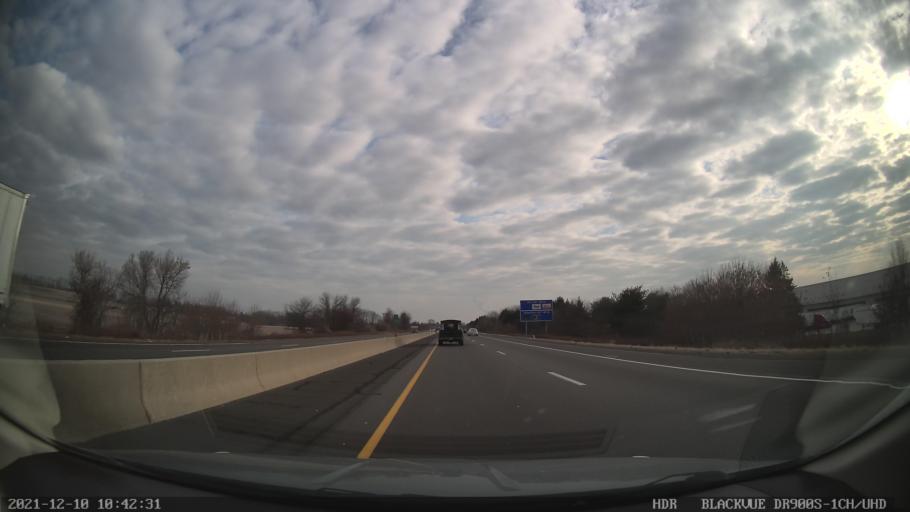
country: US
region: Pennsylvania
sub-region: Lehigh County
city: Breinigsville
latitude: 40.5768
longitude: -75.6444
